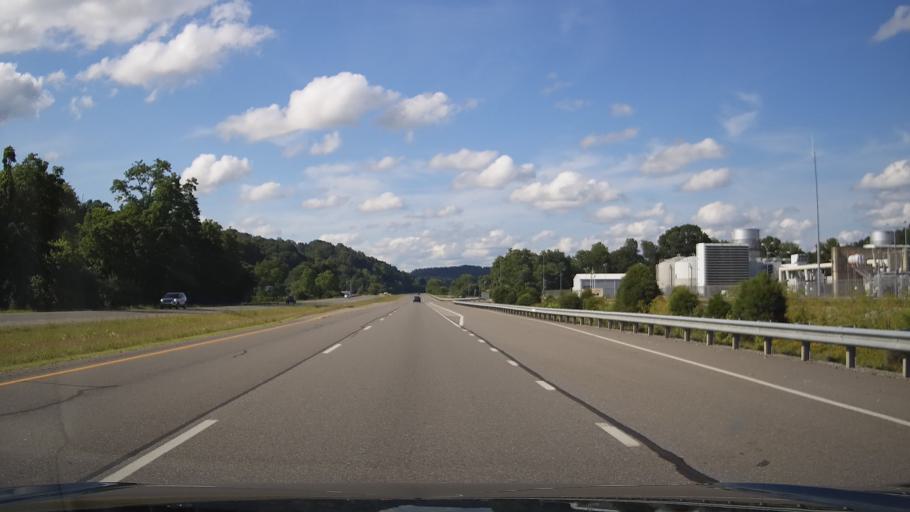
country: US
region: Kentucky
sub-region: Lawrence County
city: Louisa
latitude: 38.1910
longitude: -82.6061
